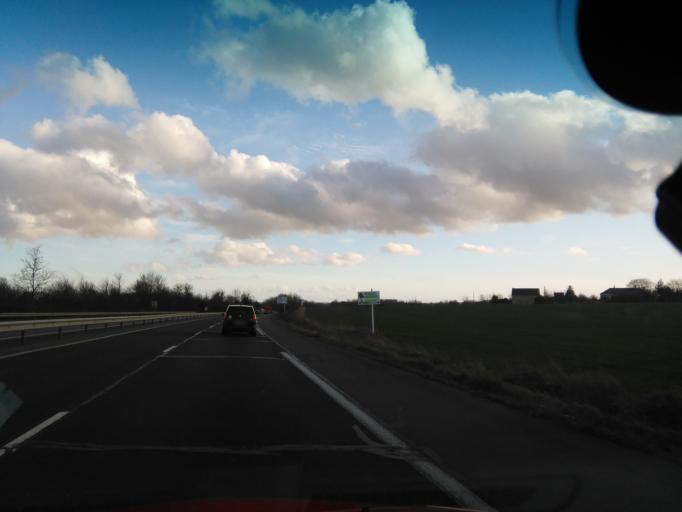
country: FR
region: Lower Normandy
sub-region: Departement du Calvados
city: Potigny
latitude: 48.9611
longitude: -0.2281
